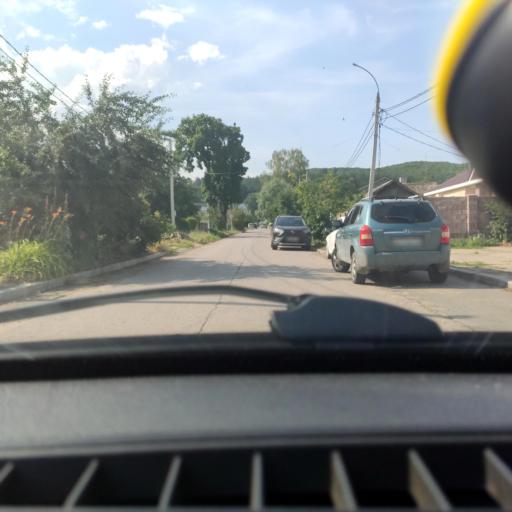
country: RU
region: Samara
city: Zhigulevsk
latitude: 53.4048
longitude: 49.4832
